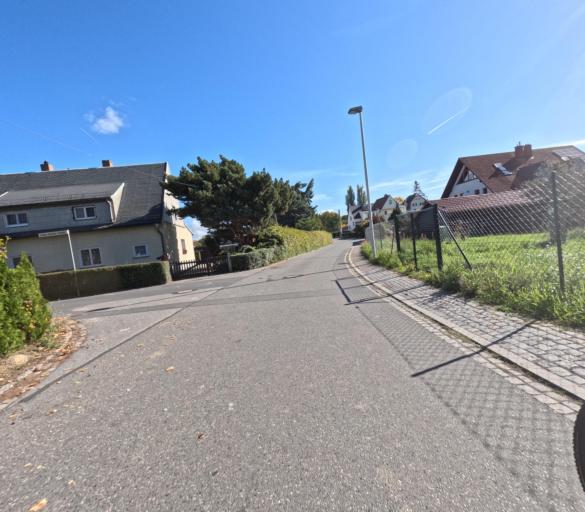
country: DE
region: Saxony
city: Radebeul
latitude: 51.1152
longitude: 13.6814
